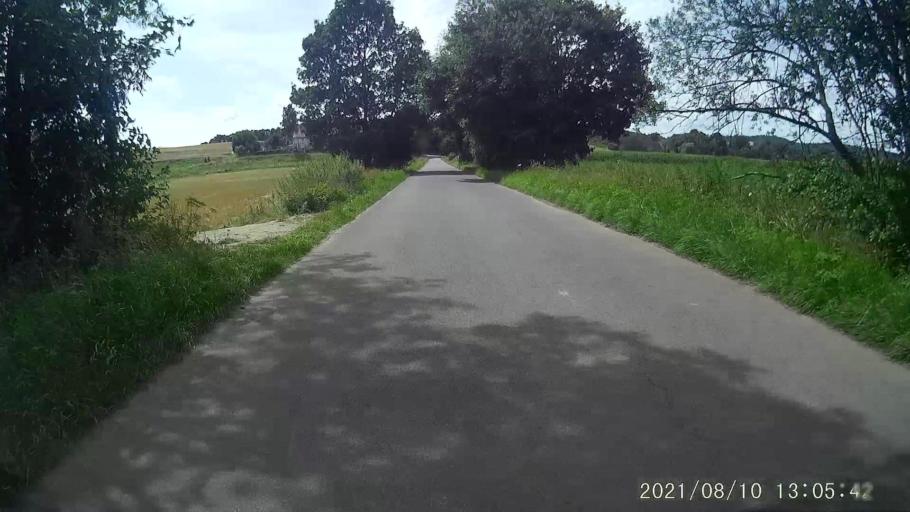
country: PL
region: Lower Silesian Voivodeship
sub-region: Powiat klodzki
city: Bozkow
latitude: 50.4832
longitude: 16.5660
